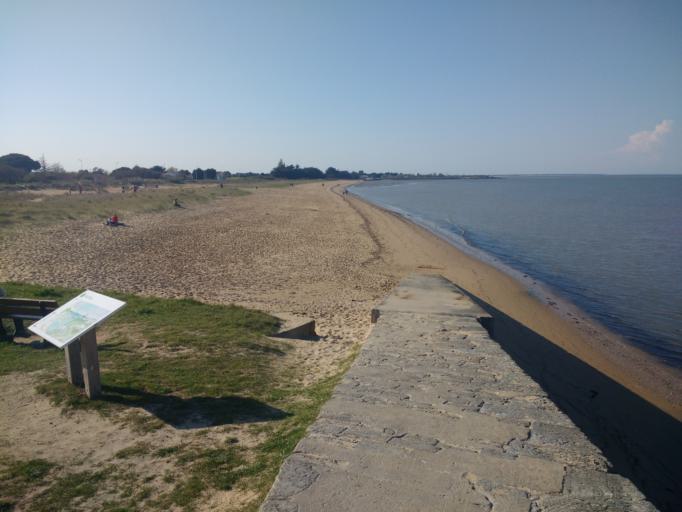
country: FR
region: Poitou-Charentes
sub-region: Departement de la Charente-Maritime
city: Saint-Trojan-les-Bains
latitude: 45.8906
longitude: -1.1947
